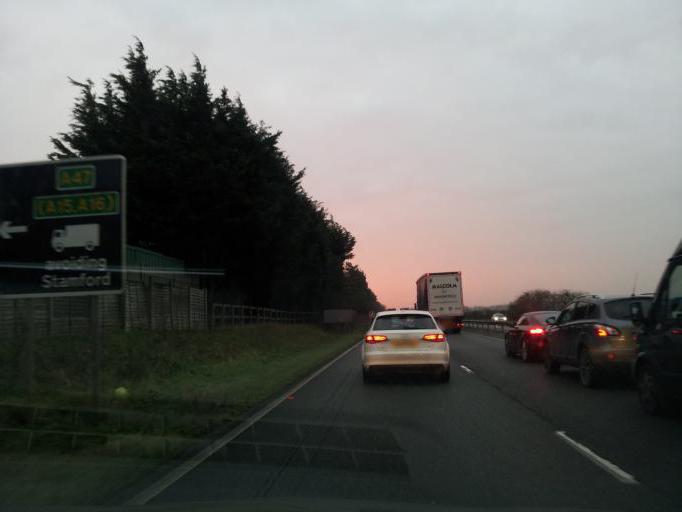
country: GB
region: England
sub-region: Peterborough
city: Thornhaugh
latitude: 52.5969
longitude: -0.4201
